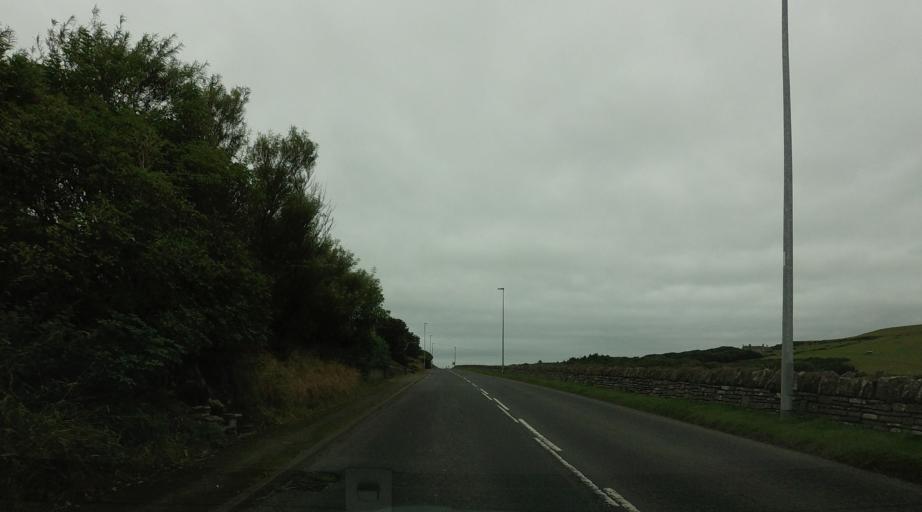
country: GB
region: Scotland
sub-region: Orkney Islands
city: Orkney
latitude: 59.0084
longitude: -3.1266
